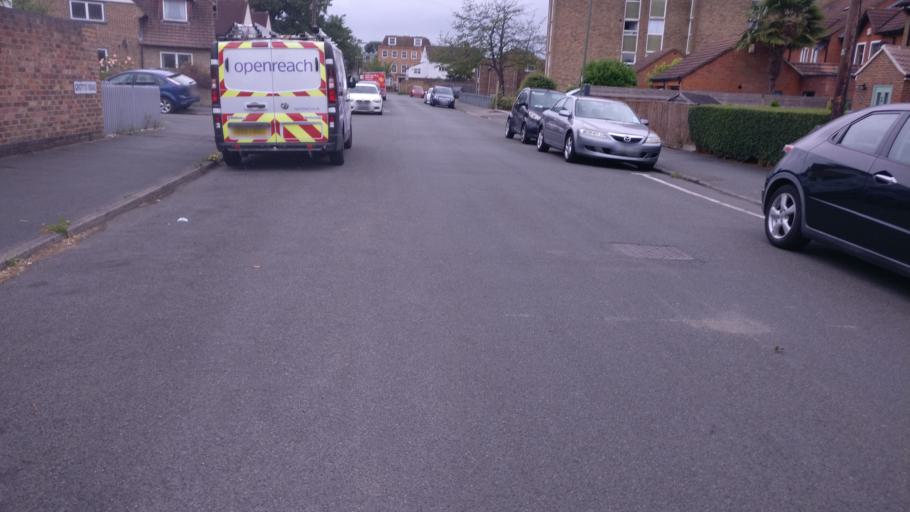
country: GB
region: England
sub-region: Surrey
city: Weybridge
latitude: 51.3760
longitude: -0.4526
